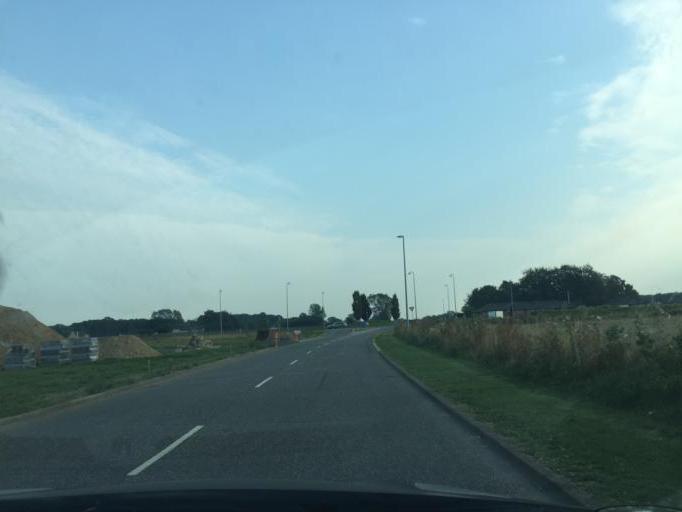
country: DK
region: South Denmark
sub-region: Kerteminde Kommune
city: Langeskov
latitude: 55.3099
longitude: 10.5944
